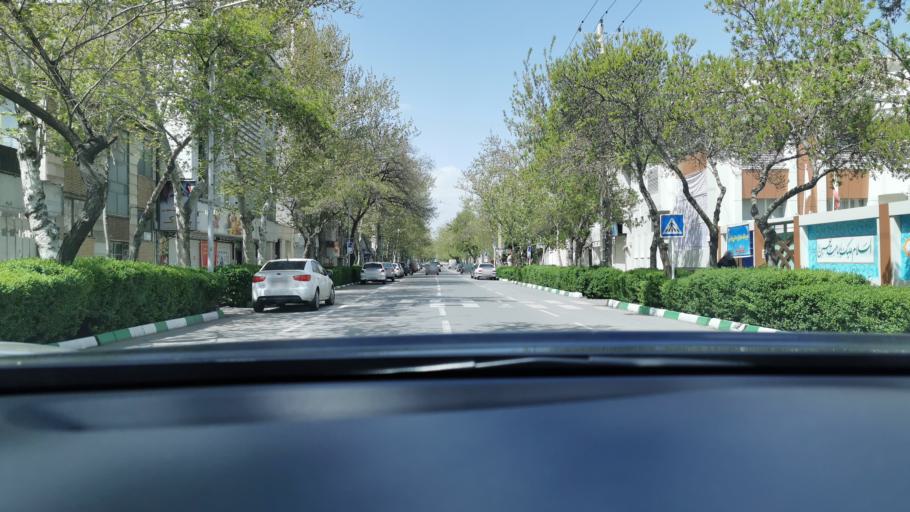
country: IR
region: Razavi Khorasan
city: Mashhad
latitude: 36.2964
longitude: 59.5972
